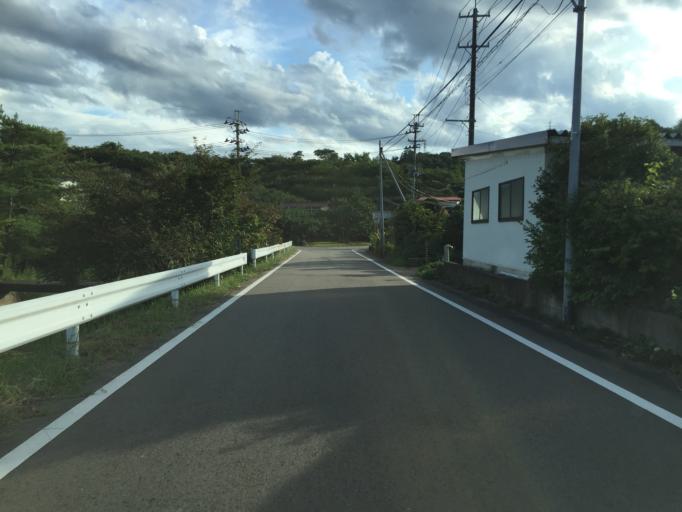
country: JP
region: Fukushima
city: Hobaramachi
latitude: 37.8069
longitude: 140.5434
